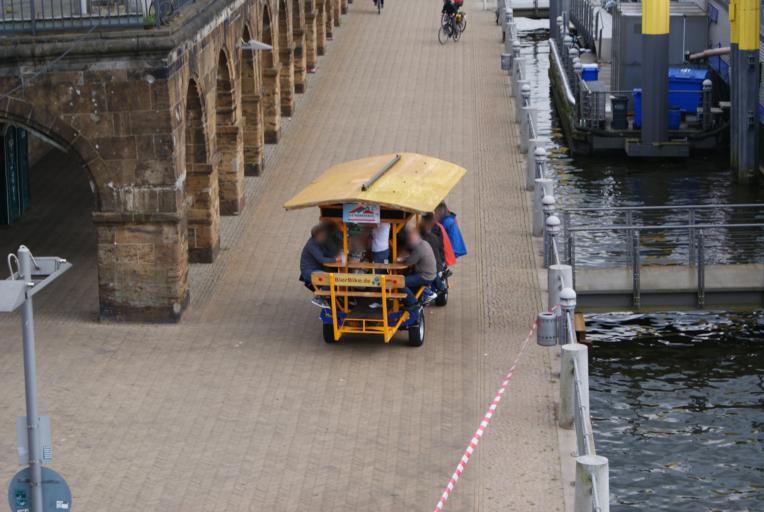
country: DE
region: Bremen
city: Bremen
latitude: 53.0733
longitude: 8.8060
